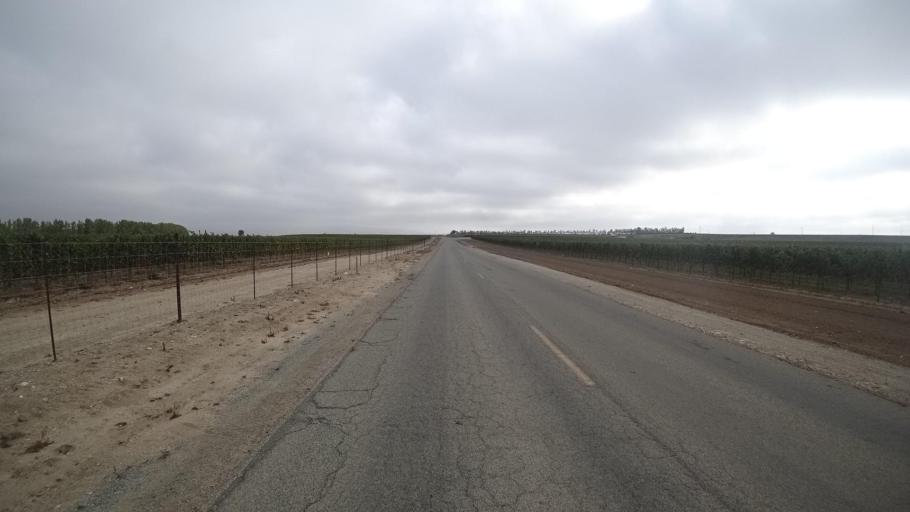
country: US
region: California
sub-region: Monterey County
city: Greenfield
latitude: 36.3250
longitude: -121.2884
